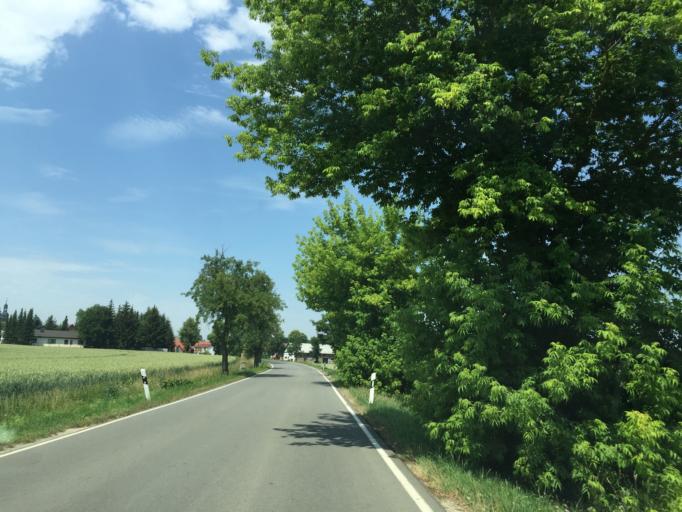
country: DE
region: Thuringia
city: Witzleben
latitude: 50.8138
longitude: 11.1411
